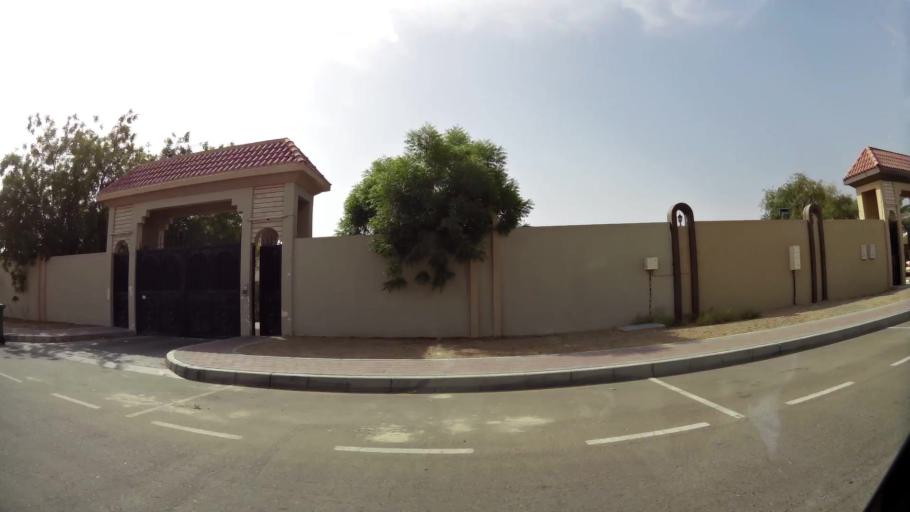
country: AE
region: Abu Dhabi
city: Al Ain
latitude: 24.1499
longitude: 55.7013
